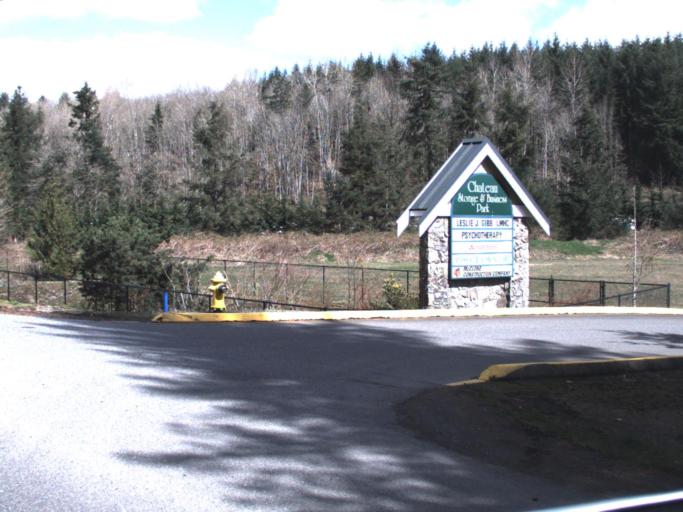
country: US
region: Washington
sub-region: King County
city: Ravensdale
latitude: 47.3456
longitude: -122.0188
